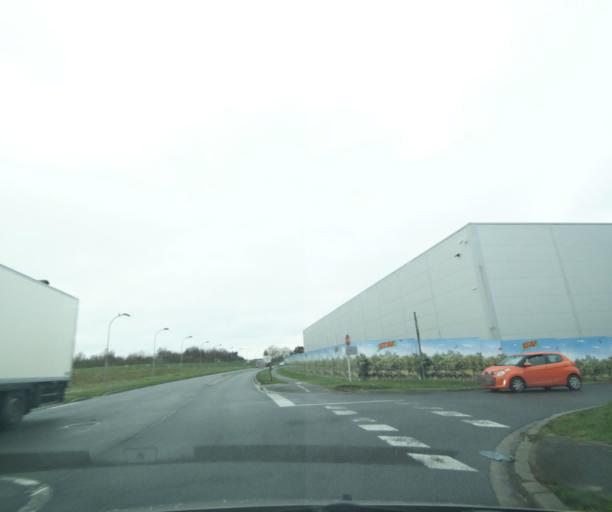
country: FR
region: Ile-de-France
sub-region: Departement du Val-de-Marne
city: Villeneuve-le-Roi
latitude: 48.7287
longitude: 2.4063
